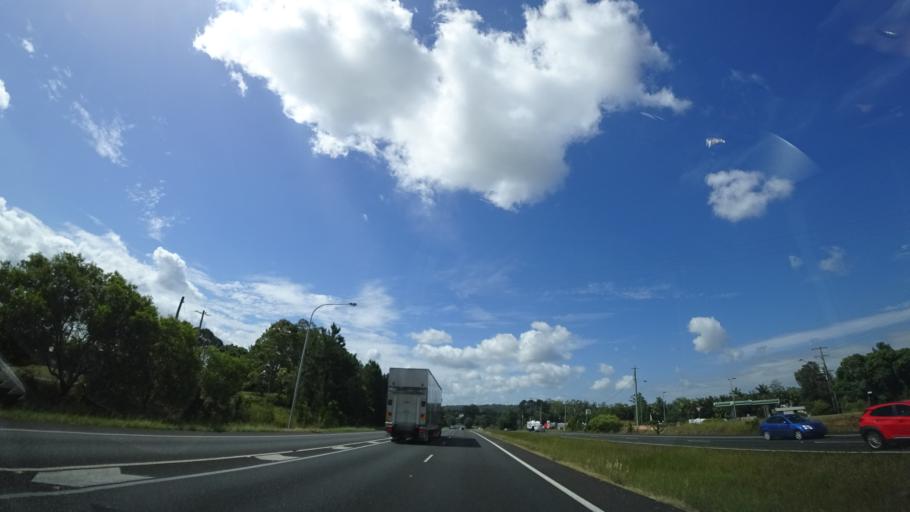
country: AU
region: Queensland
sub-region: Sunshine Coast
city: Woombye
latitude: -26.6860
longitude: 153.0036
